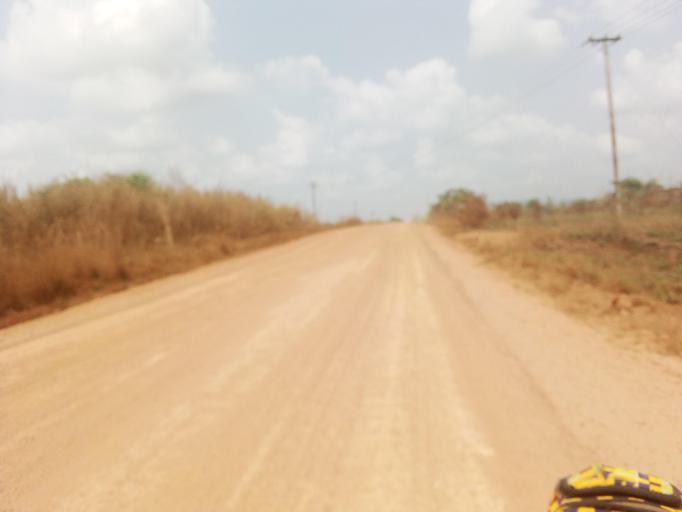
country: SL
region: Southern Province
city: Mogbwemo
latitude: 7.6707
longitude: -12.2791
